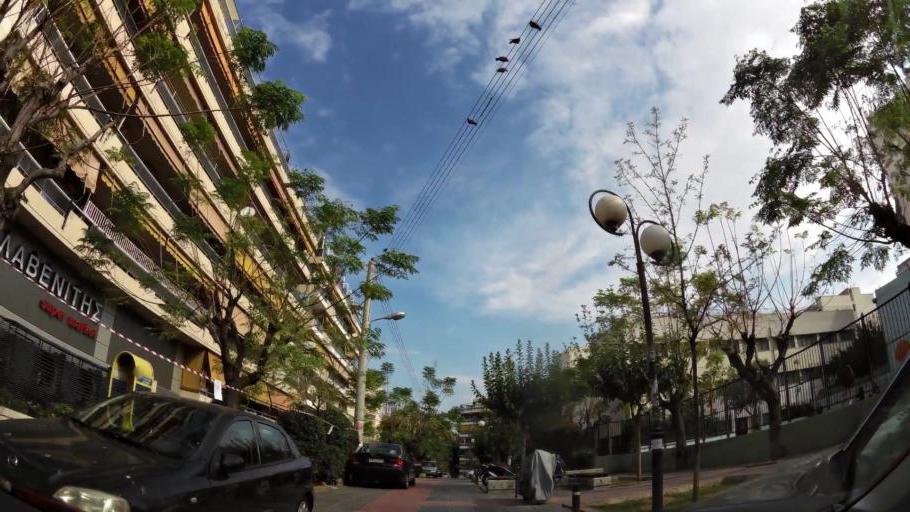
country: GR
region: Attica
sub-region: Nomarchia Athinas
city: Nea Smyrni
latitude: 37.9511
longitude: 23.7187
